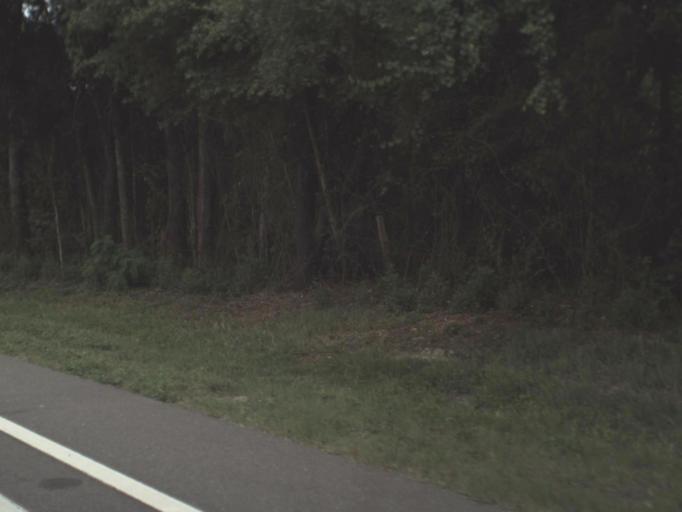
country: US
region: Florida
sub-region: Levy County
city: Chiefland
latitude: 29.4966
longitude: -82.8784
